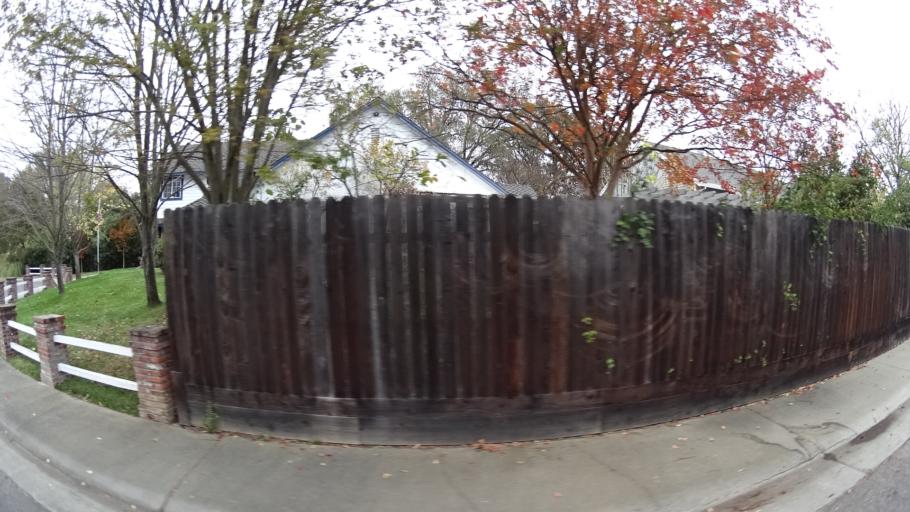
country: US
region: California
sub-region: Sacramento County
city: Citrus Heights
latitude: 38.7022
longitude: -121.3013
